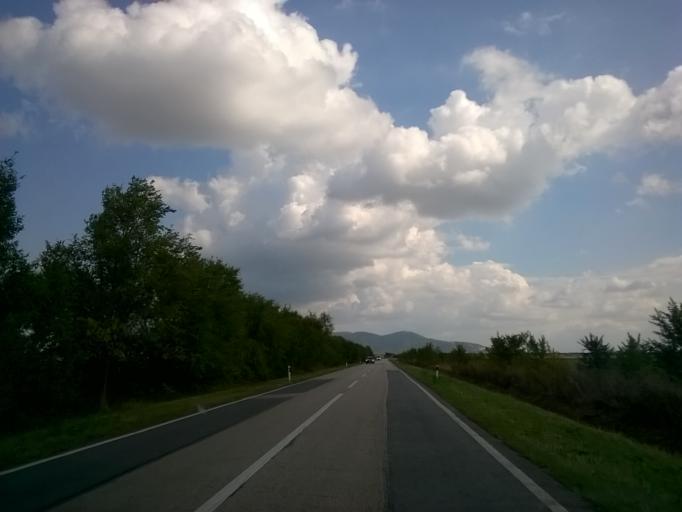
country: RS
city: Pavlis
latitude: 45.1561
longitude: 21.2494
